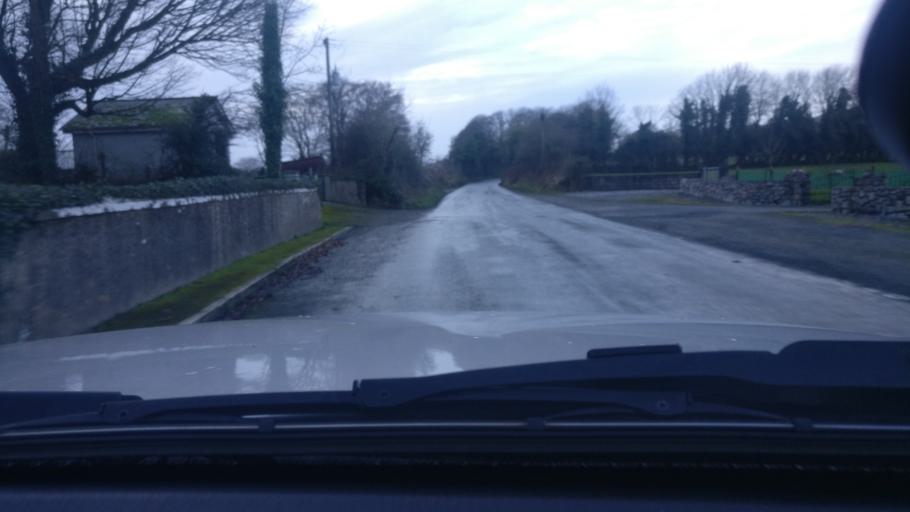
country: IE
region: Connaught
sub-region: County Galway
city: Loughrea
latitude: 53.1626
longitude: -8.5230
